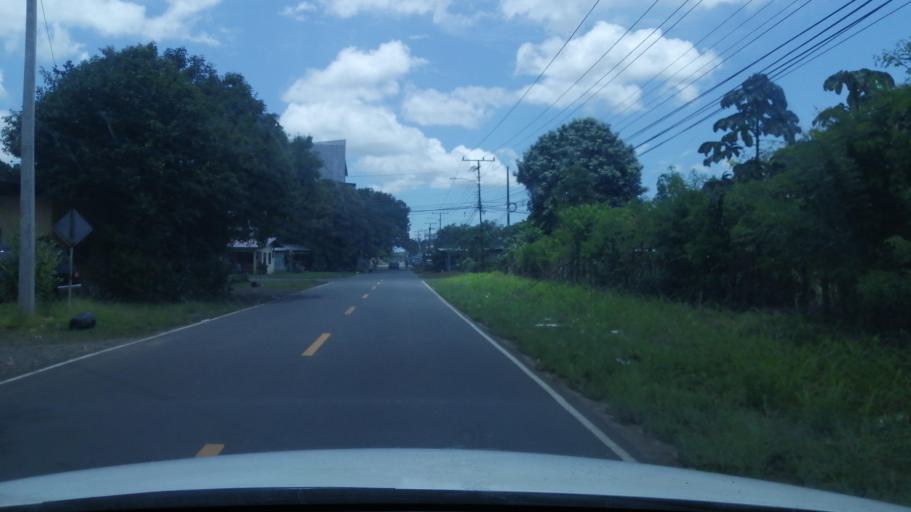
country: PA
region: Chiriqui
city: David
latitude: 8.4330
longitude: -82.4316
